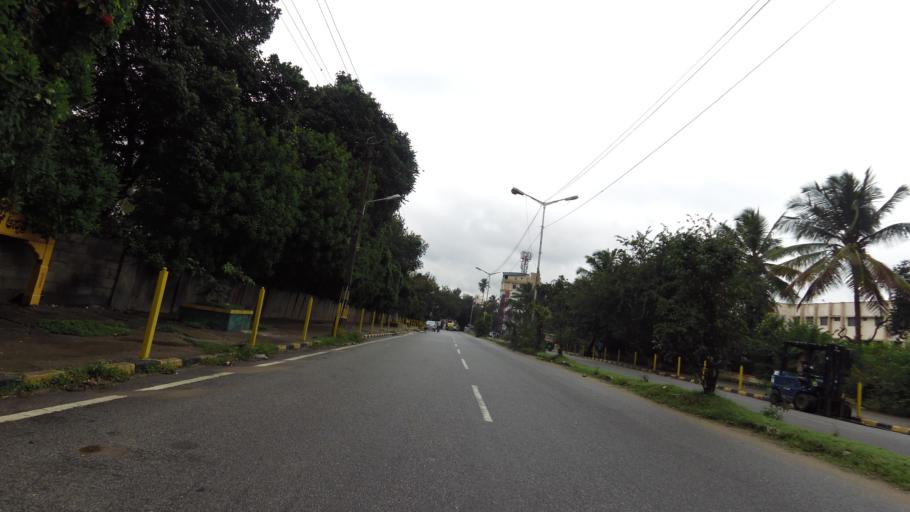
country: IN
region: Karnataka
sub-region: Bangalore Urban
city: Bangalore
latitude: 12.9835
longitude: 77.6456
